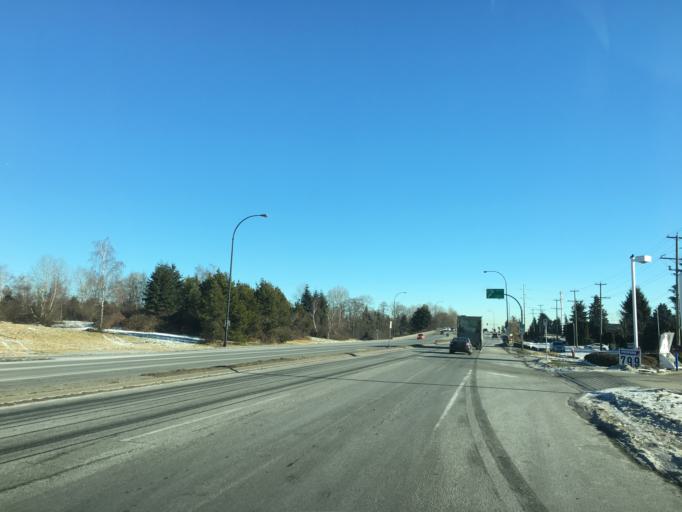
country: CA
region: British Columbia
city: Richmond
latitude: 49.1702
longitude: -123.0914
